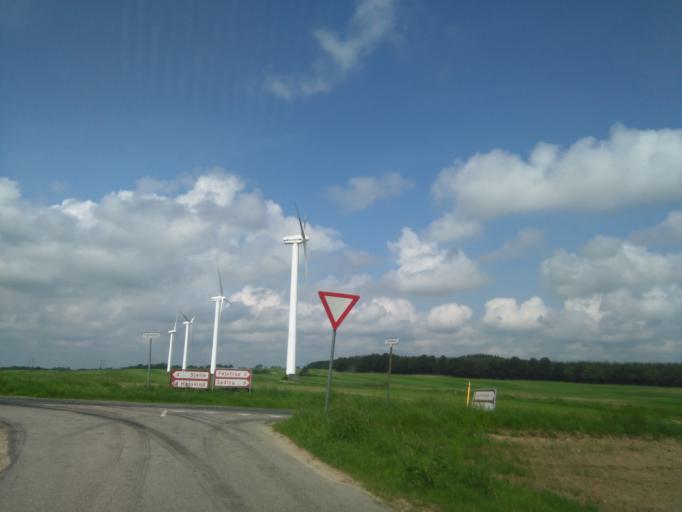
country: DK
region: Central Jutland
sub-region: Skanderborg Kommune
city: Galten
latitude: 56.2133
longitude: 9.9296
